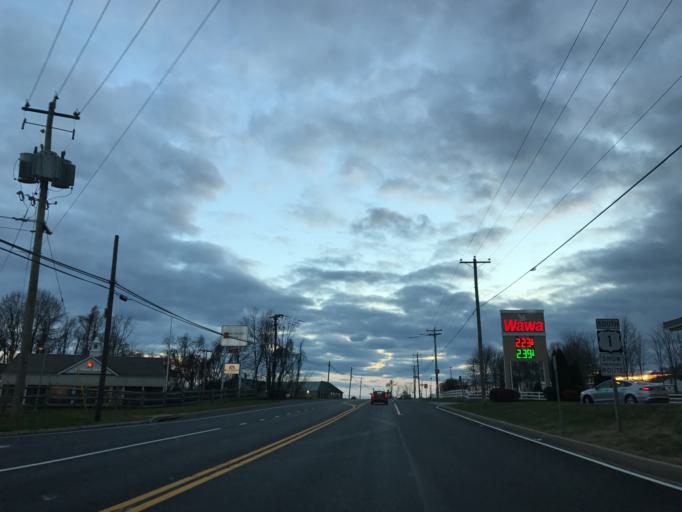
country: US
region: Maryland
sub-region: Harford County
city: South Bel Air
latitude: 39.6379
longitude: -76.2674
